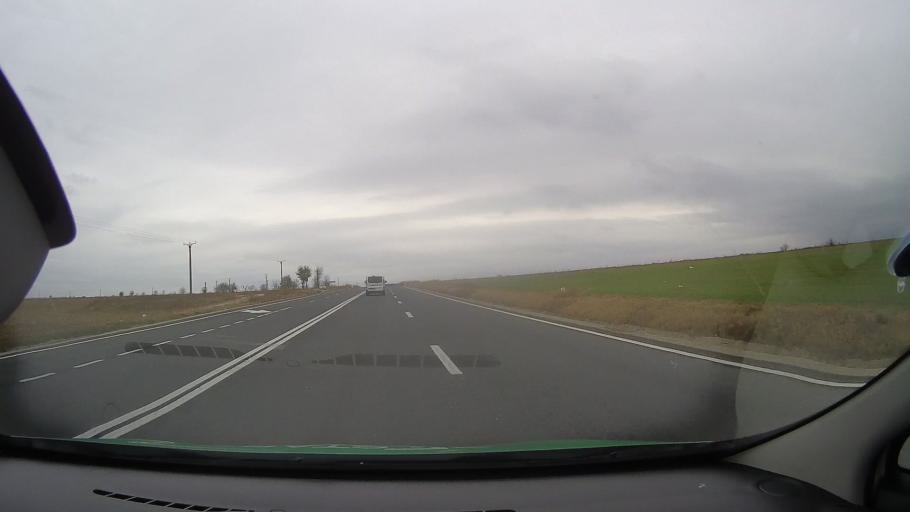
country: RO
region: Constanta
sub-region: Comuna Nicolae Balcescu
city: Nicolae Balcescu
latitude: 44.3827
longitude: 28.4007
